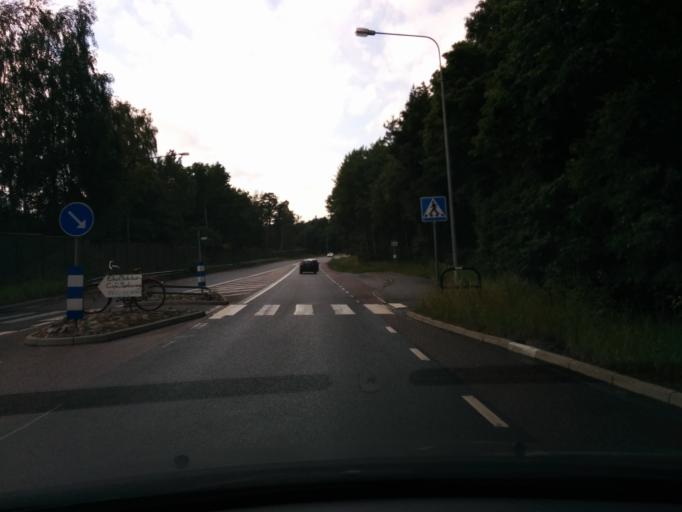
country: SE
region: Stockholm
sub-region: Norrtalje Kommun
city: Bergshamra
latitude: 59.4190
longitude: 18.0071
